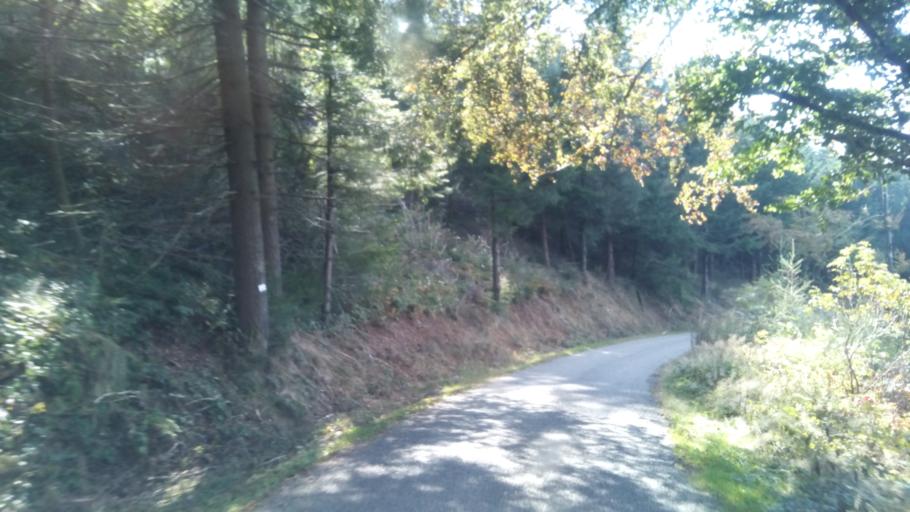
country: FR
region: Bourgogne
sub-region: Departement de Saone-et-Loire
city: Matour
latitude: 46.2011
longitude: 4.4865
